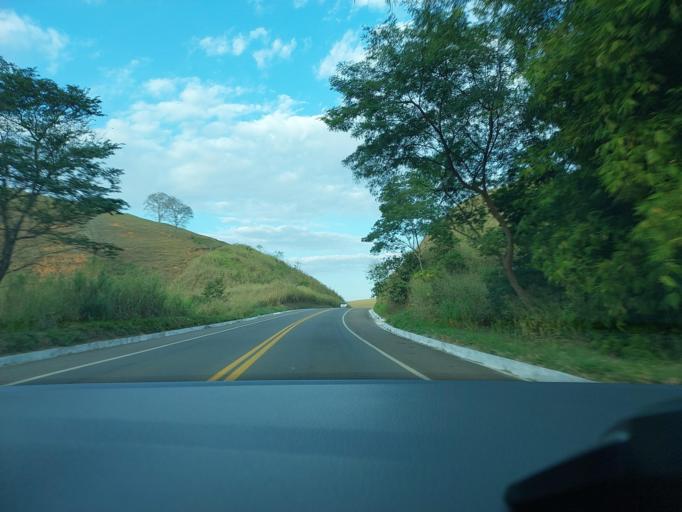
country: BR
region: Minas Gerais
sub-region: Muriae
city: Muriae
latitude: -21.1377
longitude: -42.3104
